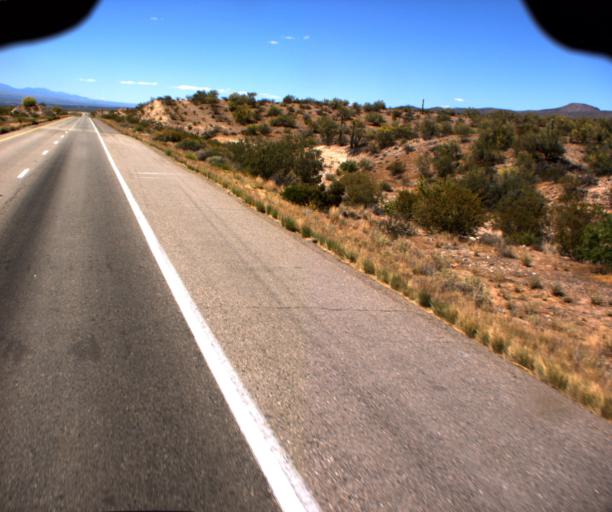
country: US
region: Arizona
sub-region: Yavapai County
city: Bagdad
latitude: 34.5987
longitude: -113.5178
